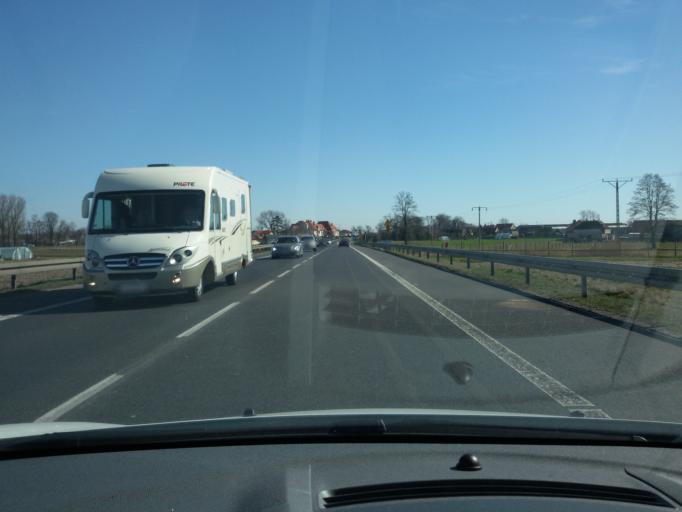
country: PL
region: Greater Poland Voivodeship
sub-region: Powiat leszczynski
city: Rydzyna
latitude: 51.7827
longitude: 16.6647
